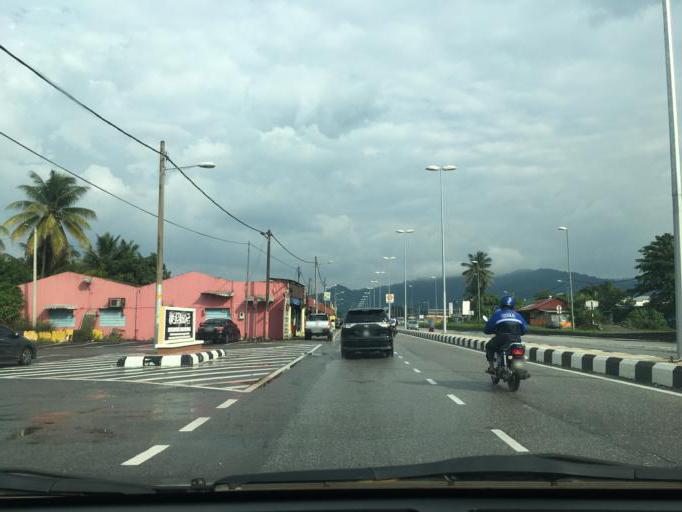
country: MY
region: Selangor
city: Rawang
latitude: 3.3145
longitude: 101.5787
